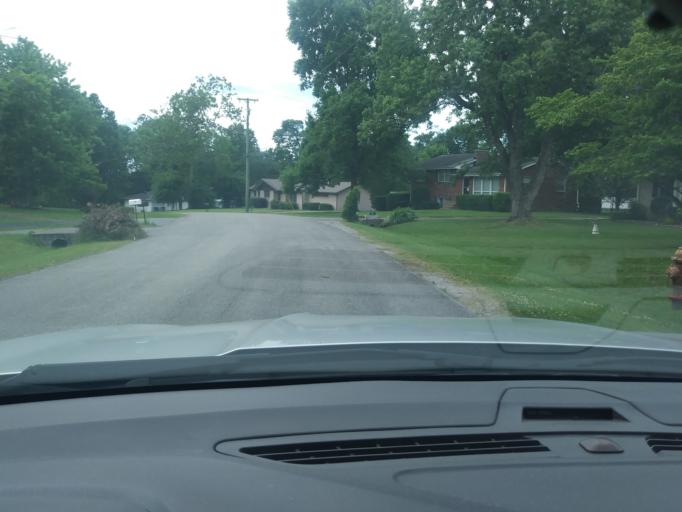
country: US
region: Tennessee
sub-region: Davidson County
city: Nashville
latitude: 36.1290
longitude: -86.7210
